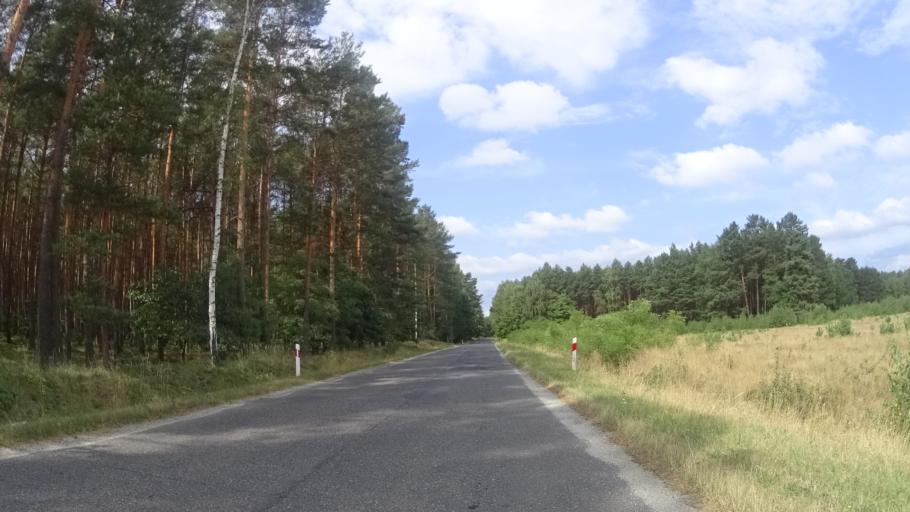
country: PL
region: Lubusz
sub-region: Powiat zarski
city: Leknica
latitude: 51.5407
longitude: 14.7908
